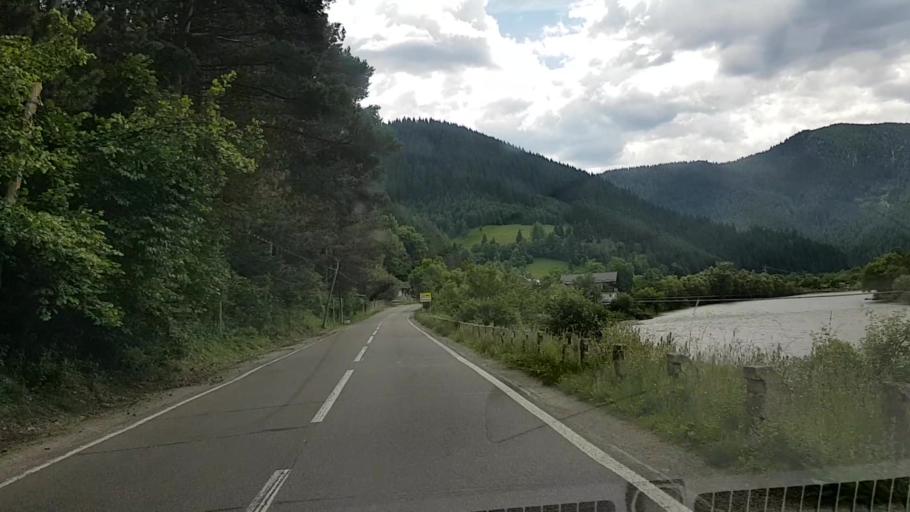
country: RO
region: Suceava
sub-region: Comuna Brosteni
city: Brosteni
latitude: 47.2331
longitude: 25.7437
